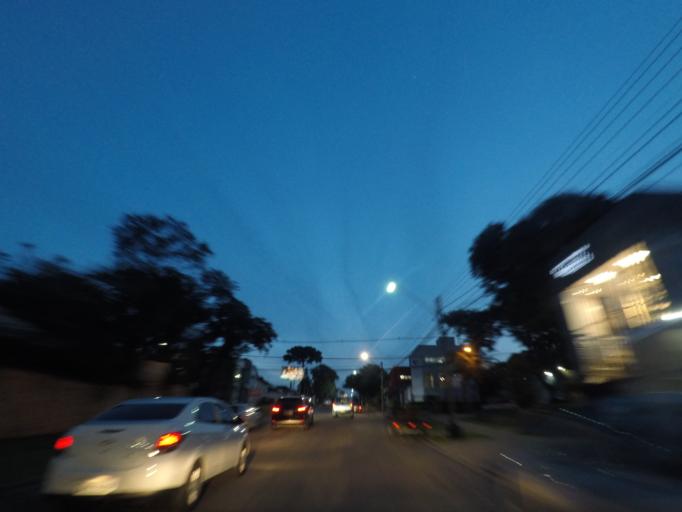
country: BR
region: Parana
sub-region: Curitiba
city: Curitiba
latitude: -25.4396
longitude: -49.2966
